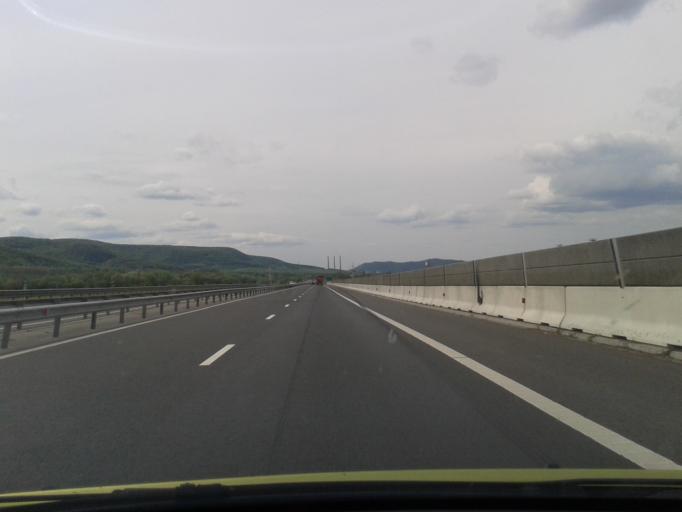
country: RO
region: Hunedoara
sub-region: Comuna Soimus
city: Soimus
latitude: 45.9101
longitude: 22.9072
